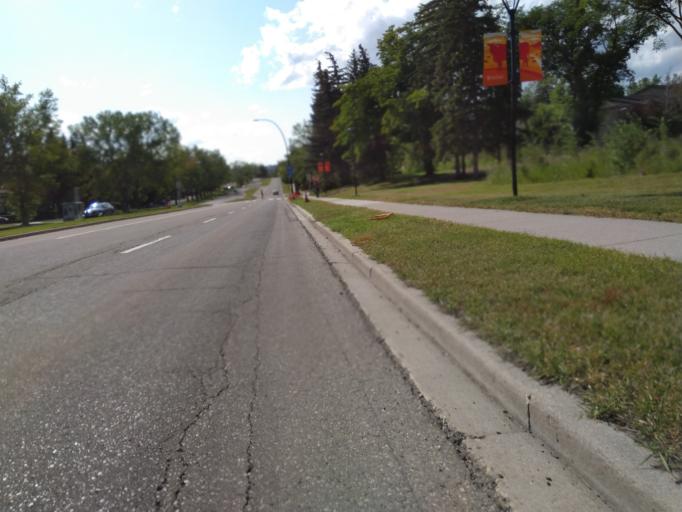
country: CA
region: Alberta
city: Calgary
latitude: 51.0745
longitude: -114.1342
